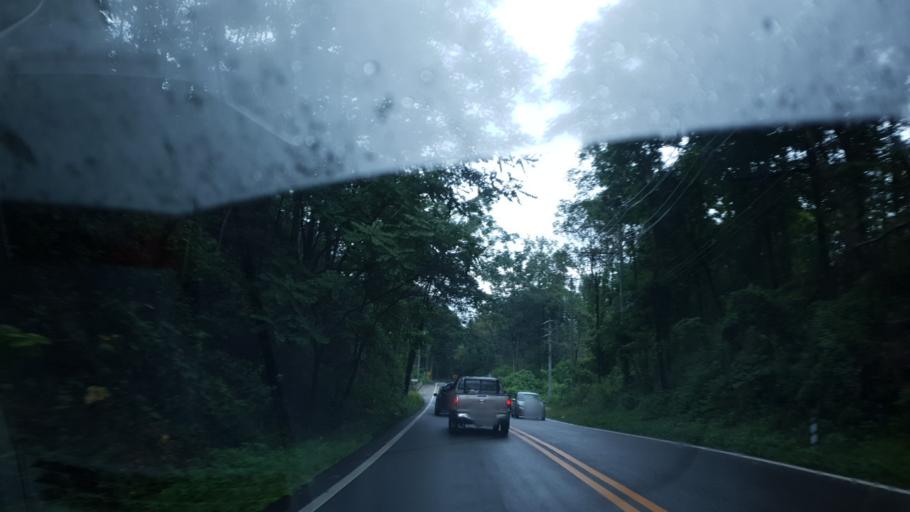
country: TH
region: Chiang Mai
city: Hot
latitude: 18.2160
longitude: 98.4461
